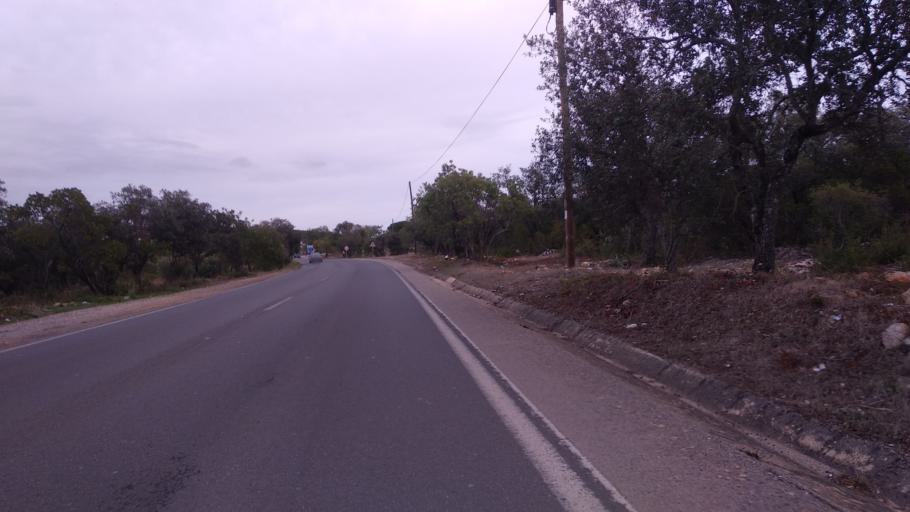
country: PT
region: Faro
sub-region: Faro
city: Santa Barbara de Nexe
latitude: 37.1496
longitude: -7.9467
